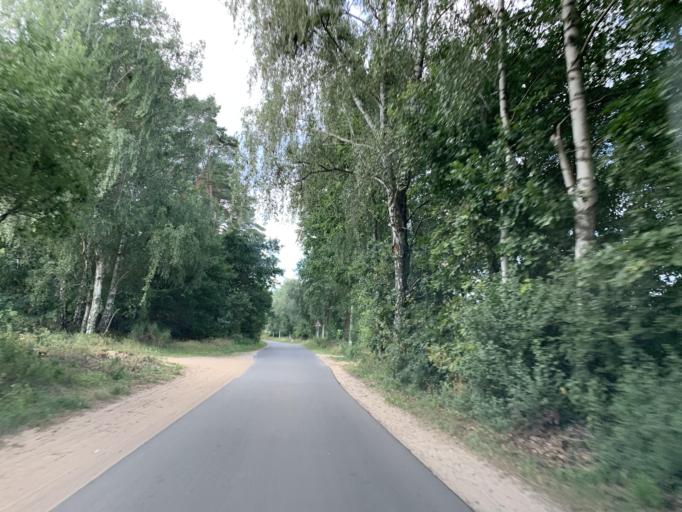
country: DE
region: Mecklenburg-Vorpommern
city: Carpin
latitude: 53.3664
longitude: 13.2524
